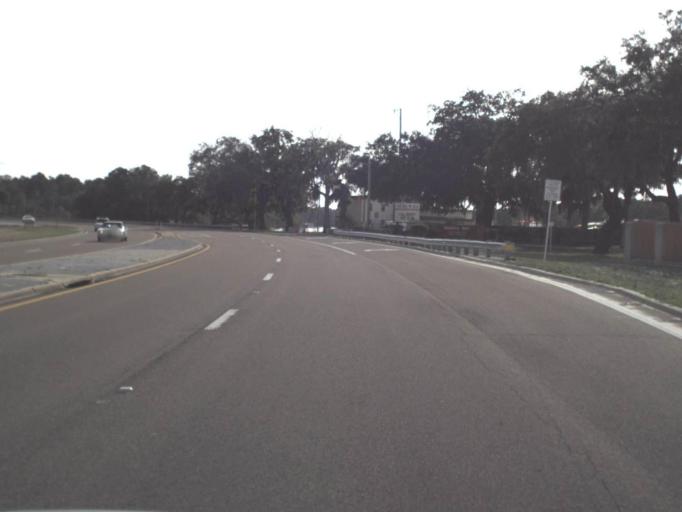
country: US
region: Florida
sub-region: Bay County
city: Tyndall Air Force Base
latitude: 30.1004
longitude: -85.6119
